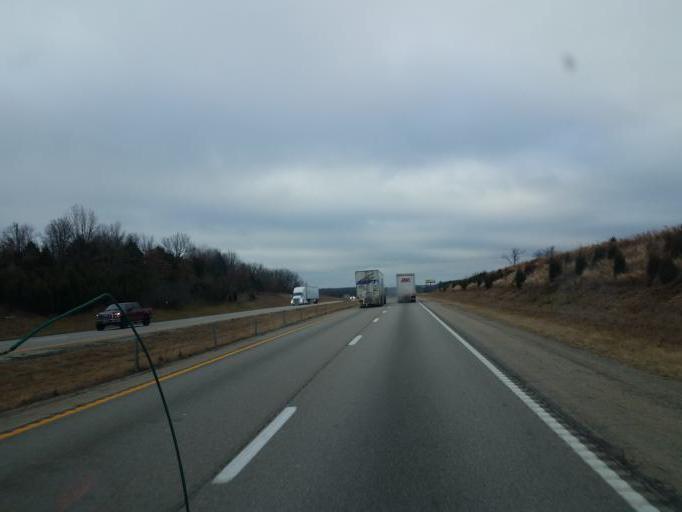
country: US
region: Missouri
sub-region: Laclede County
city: Lebanon
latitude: 37.5397
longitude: -92.8171
